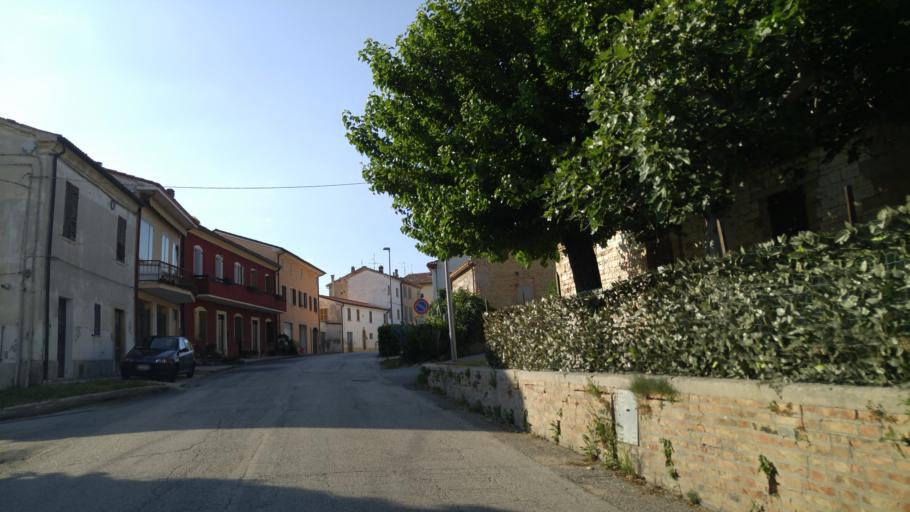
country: IT
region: The Marches
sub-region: Provincia di Pesaro e Urbino
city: Sant'Ippolito
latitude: 43.6836
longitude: 12.8712
